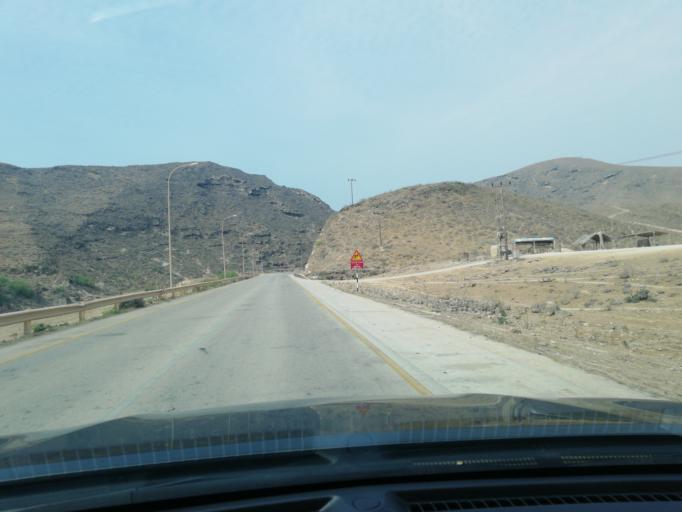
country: OM
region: Zufar
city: Salalah
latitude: 16.9013
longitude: 53.8197
